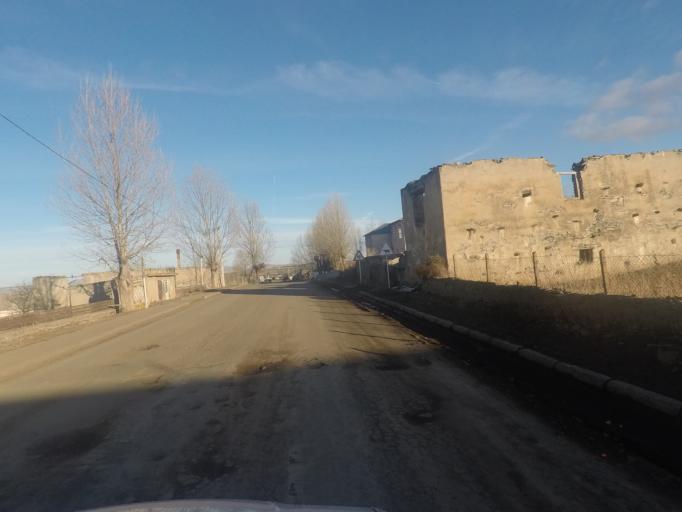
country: GE
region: Kvemo Kartli
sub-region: Tsalka
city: Tsalka
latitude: 41.5998
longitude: 44.0047
